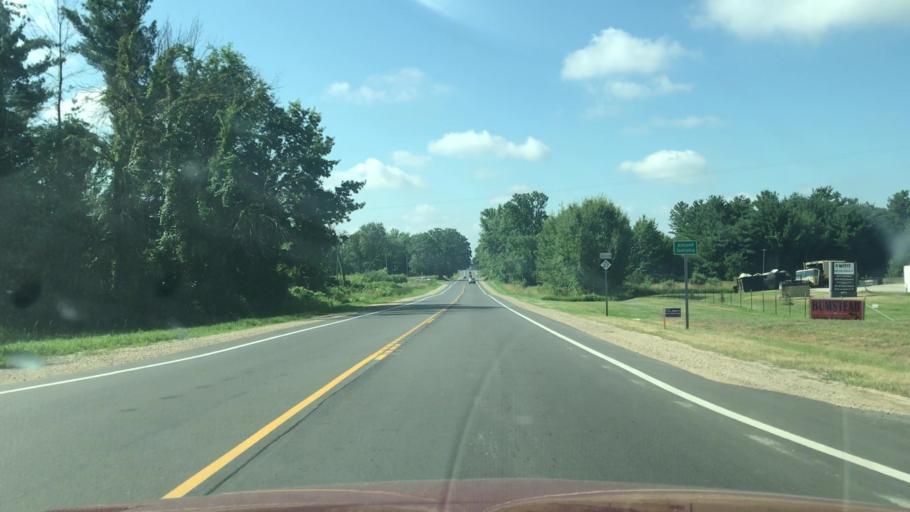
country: US
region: Michigan
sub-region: Newaygo County
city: Newaygo
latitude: 43.3801
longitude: -85.8009
